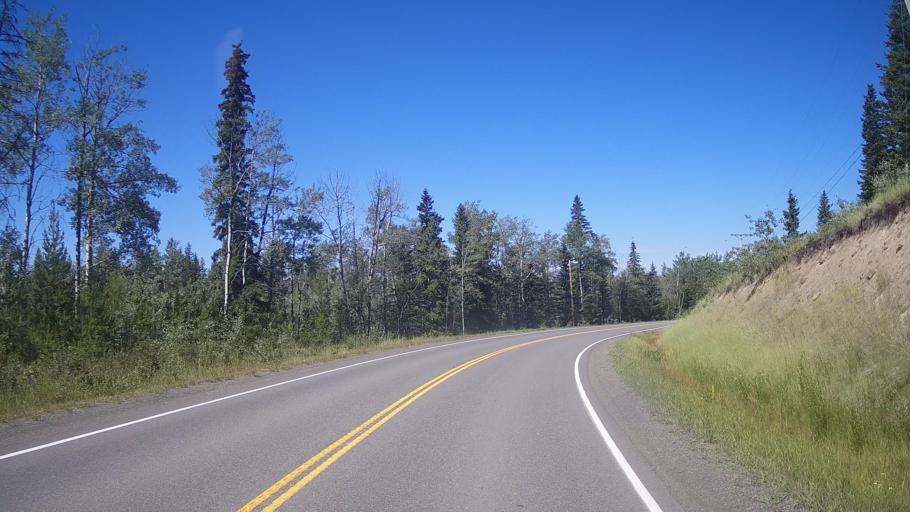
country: CA
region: British Columbia
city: Cache Creek
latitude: 51.5515
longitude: -121.1847
